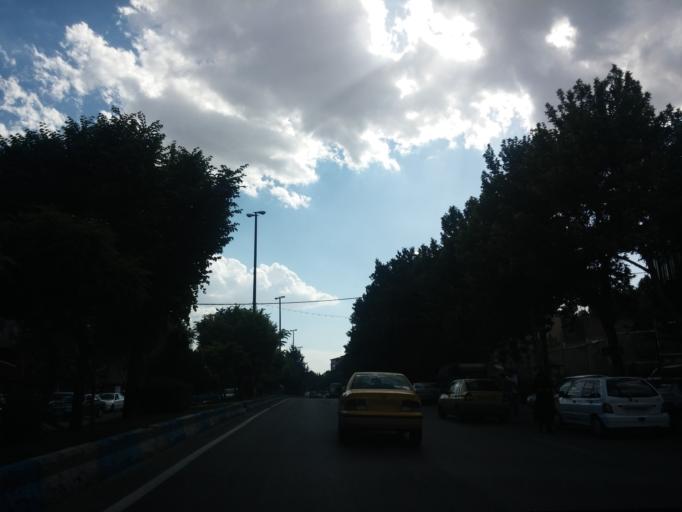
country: IR
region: Tehran
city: Damavand
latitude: 35.7364
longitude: 51.9123
